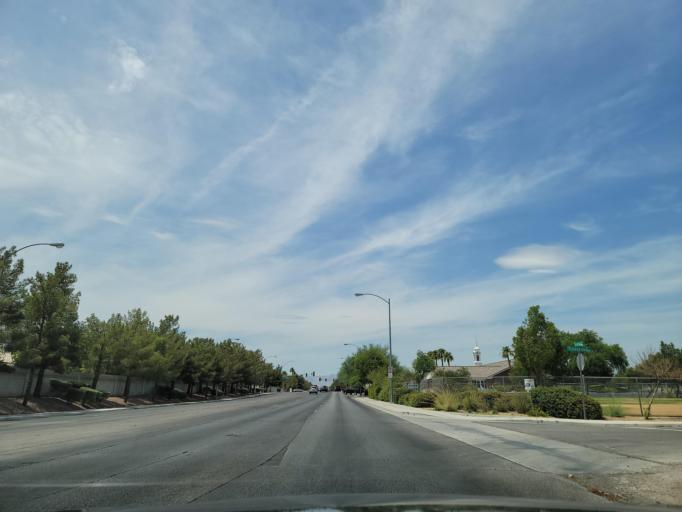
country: US
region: Nevada
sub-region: Clark County
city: Whitney
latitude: 36.0207
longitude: -115.1339
